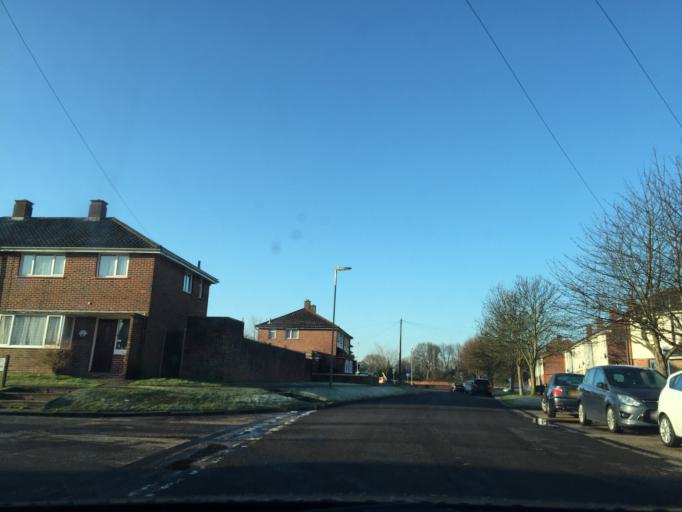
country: GB
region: England
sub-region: Hampshire
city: Lee-on-the-Solent
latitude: 50.8132
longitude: -1.1693
